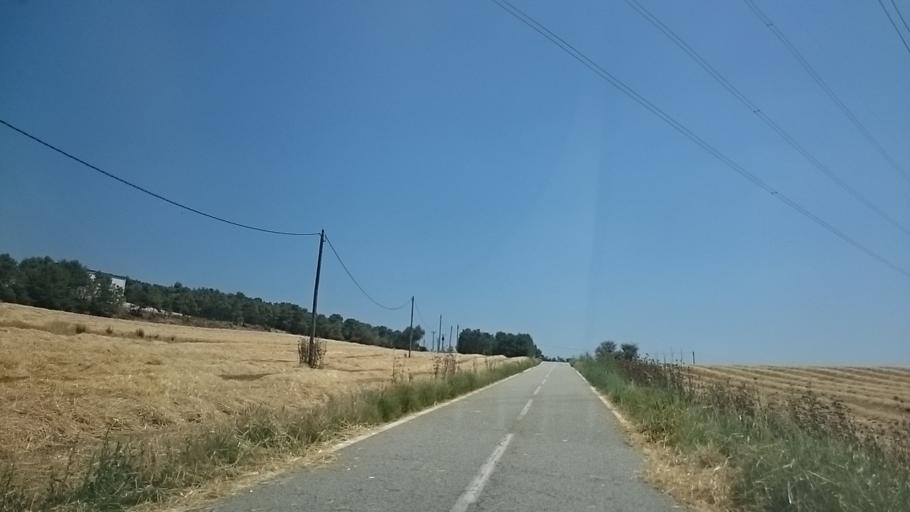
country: ES
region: Catalonia
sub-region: Provincia de Tarragona
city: Querol
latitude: 41.4528
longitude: 1.4502
